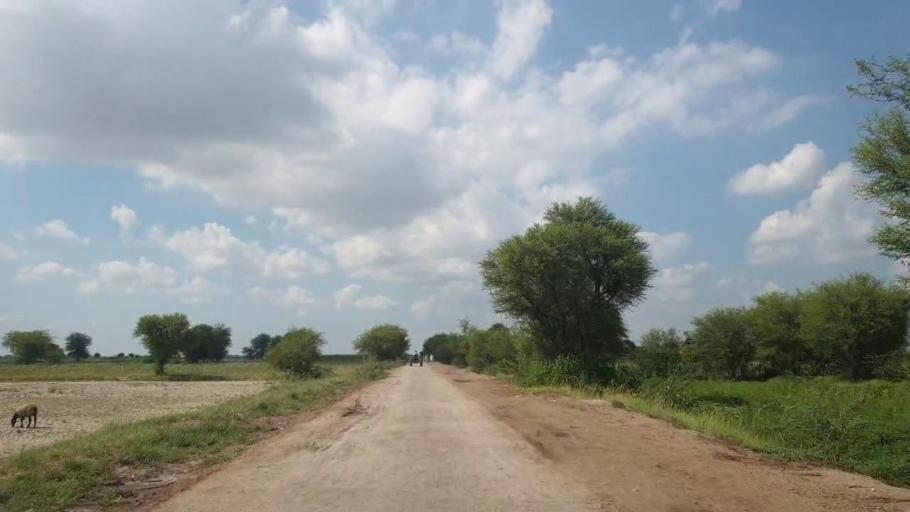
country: PK
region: Sindh
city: Pithoro
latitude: 25.5861
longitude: 69.3590
